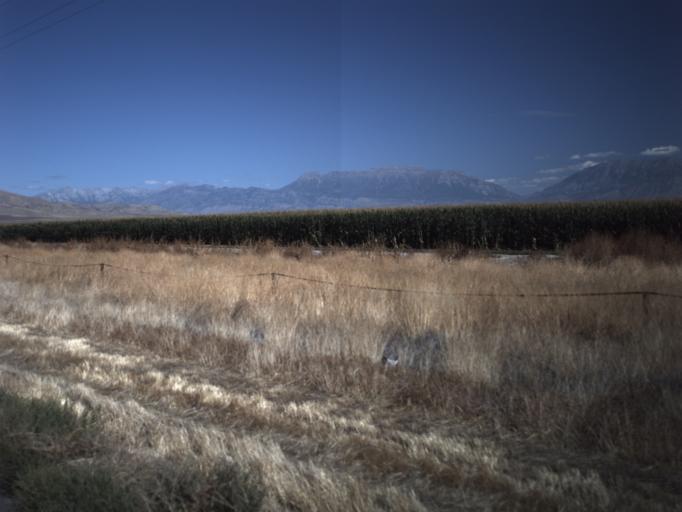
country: US
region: Utah
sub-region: Utah County
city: Genola
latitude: 40.1041
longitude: -111.9591
